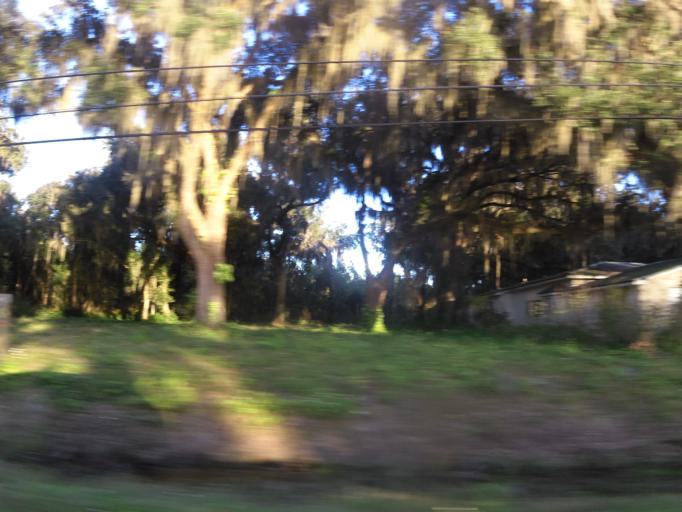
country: US
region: Florida
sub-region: Putnam County
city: East Palatka
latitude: 29.8164
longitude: -81.5506
